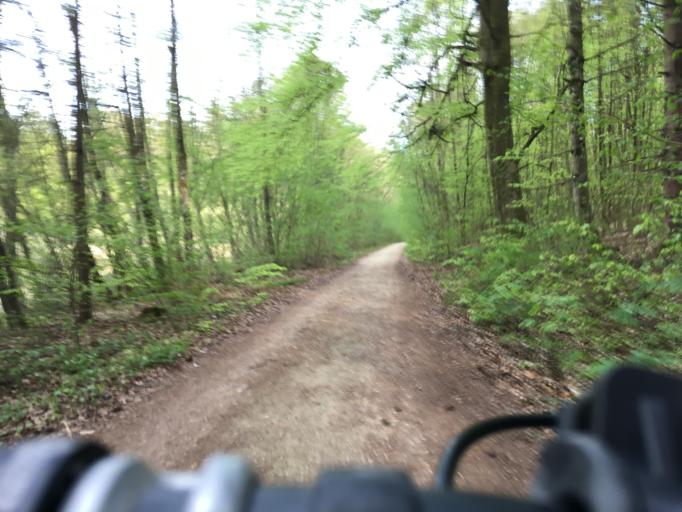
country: DE
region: Baden-Wuerttemberg
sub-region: Freiburg Region
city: Gottmadingen
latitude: 47.7408
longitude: 8.7522
